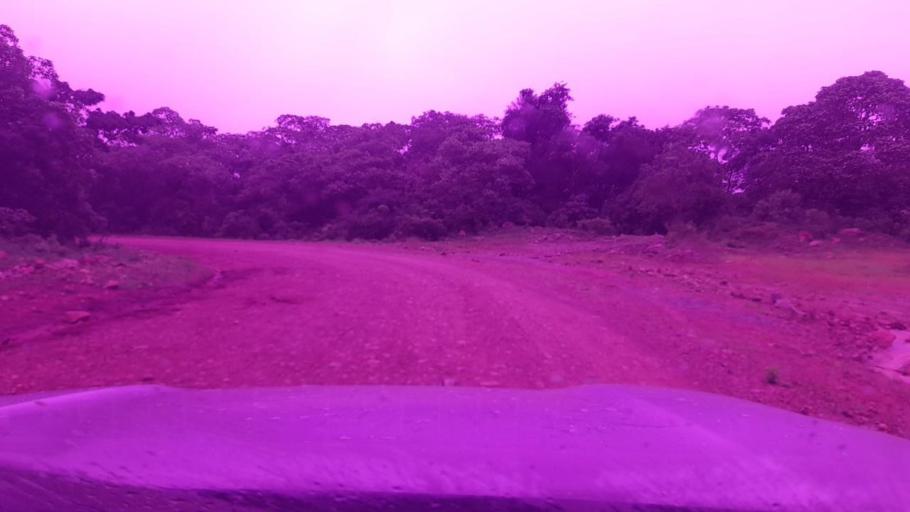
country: ET
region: Southern Nations, Nationalities, and People's Region
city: Bonga
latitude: 7.5193
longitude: 36.0580
